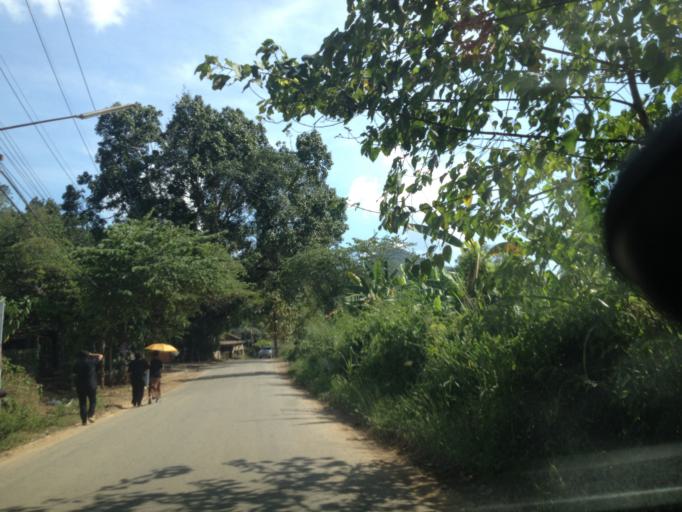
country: TH
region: Chiang Mai
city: Samoeng
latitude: 18.8604
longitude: 98.7304
